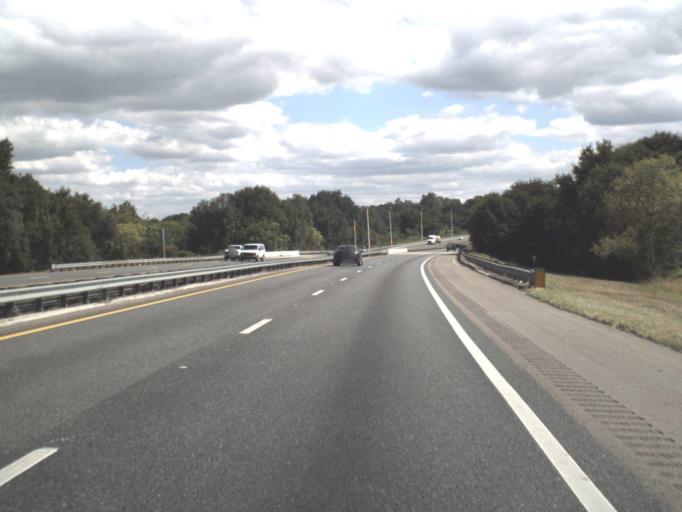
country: US
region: Florida
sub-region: Orange County
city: Oakland
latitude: 28.5531
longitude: -81.6556
